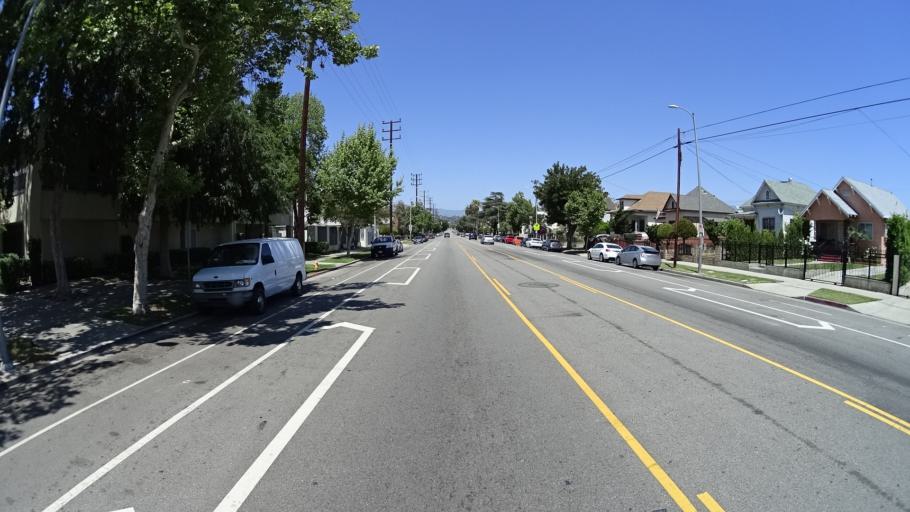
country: US
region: California
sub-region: Los Angeles County
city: Boyle Heights
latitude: 34.0685
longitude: -118.2117
